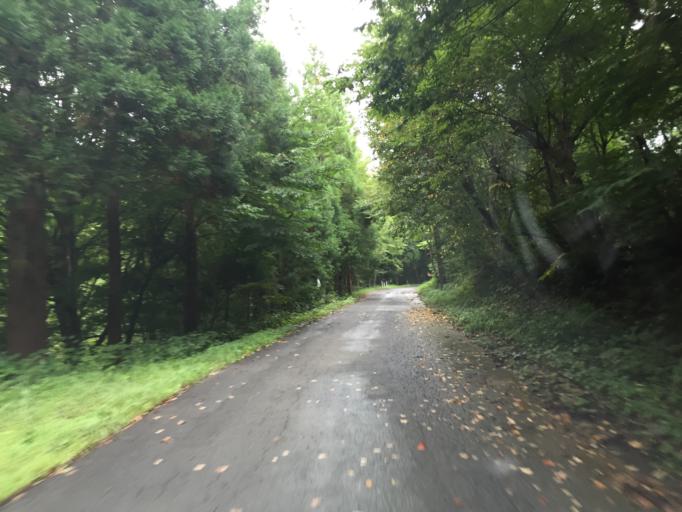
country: JP
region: Fukushima
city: Fukushima-shi
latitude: 37.8128
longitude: 140.3450
